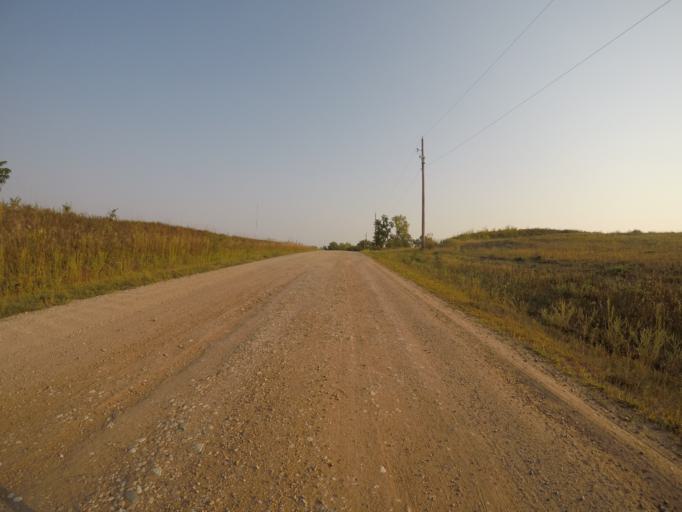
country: US
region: Kansas
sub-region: Marshall County
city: Marysville
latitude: 39.8551
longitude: -96.6480
